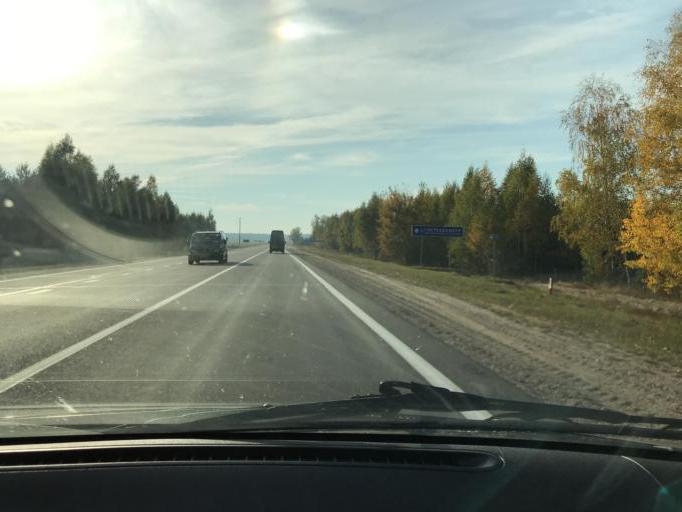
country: BY
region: Brest
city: Horad Pinsk
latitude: 52.1524
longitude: 25.9276
